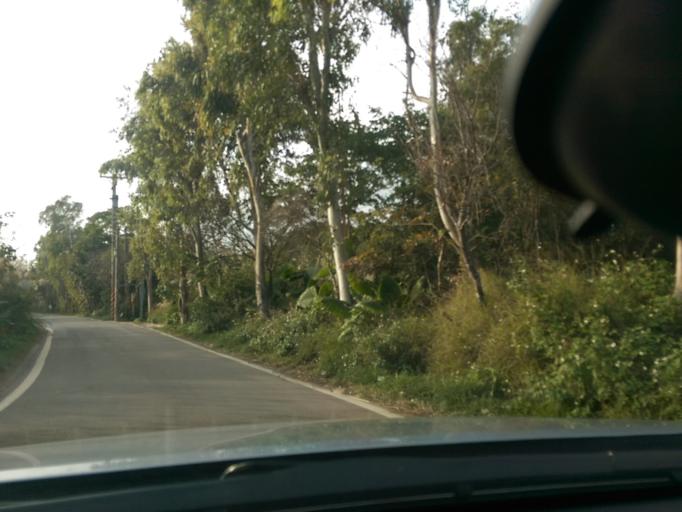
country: TW
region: Taiwan
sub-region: Taoyuan
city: Taoyuan
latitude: 25.0915
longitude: 121.3650
